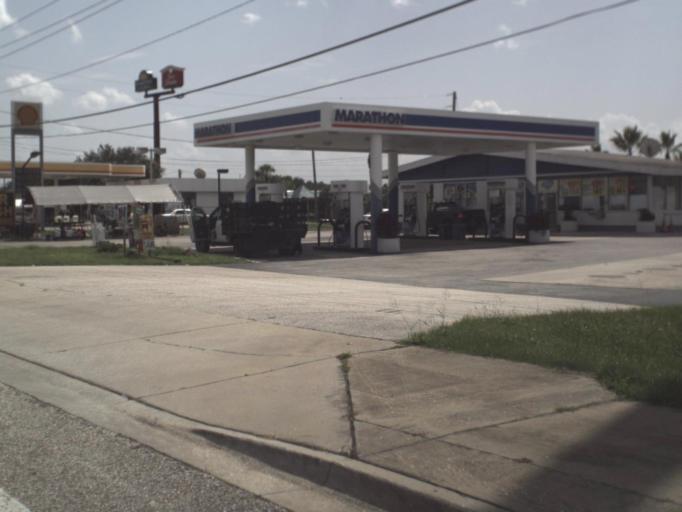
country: US
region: Florida
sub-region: Polk County
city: Loughman
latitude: 28.2317
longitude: -81.6496
